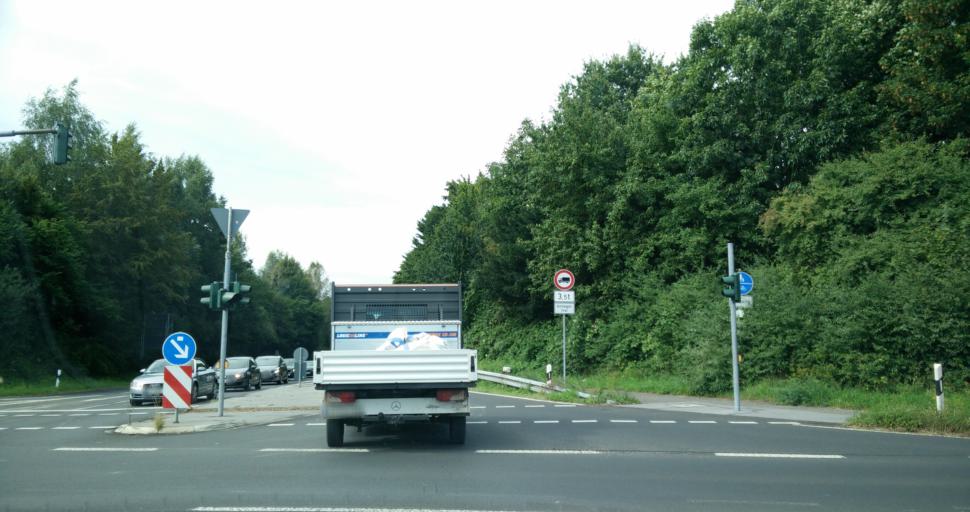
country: DE
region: North Rhine-Westphalia
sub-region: Regierungsbezirk Dusseldorf
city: Mettmann
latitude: 51.2558
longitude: 6.9496
